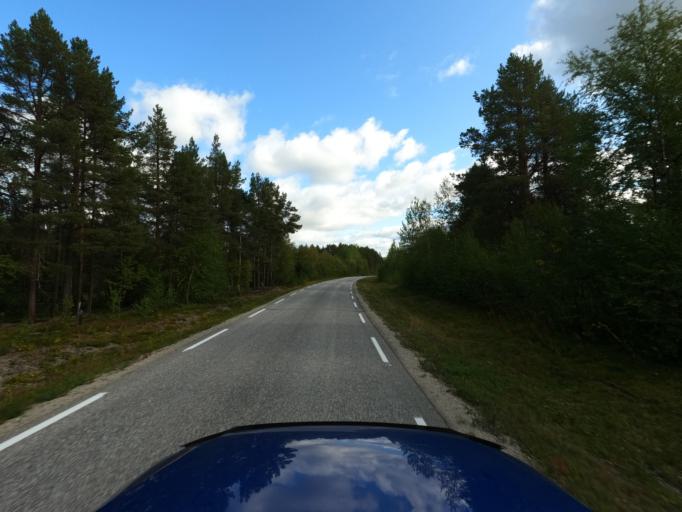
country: NO
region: Finnmark Fylke
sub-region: Karasjok
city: Karasjohka
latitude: 69.4325
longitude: 25.1355
